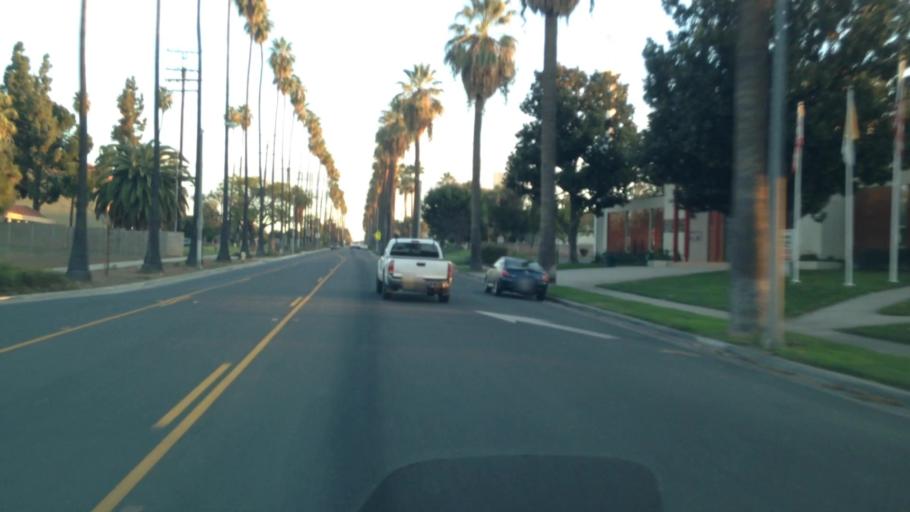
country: US
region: California
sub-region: Riverside County
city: Riverside
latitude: 33.9239
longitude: -117.4386
